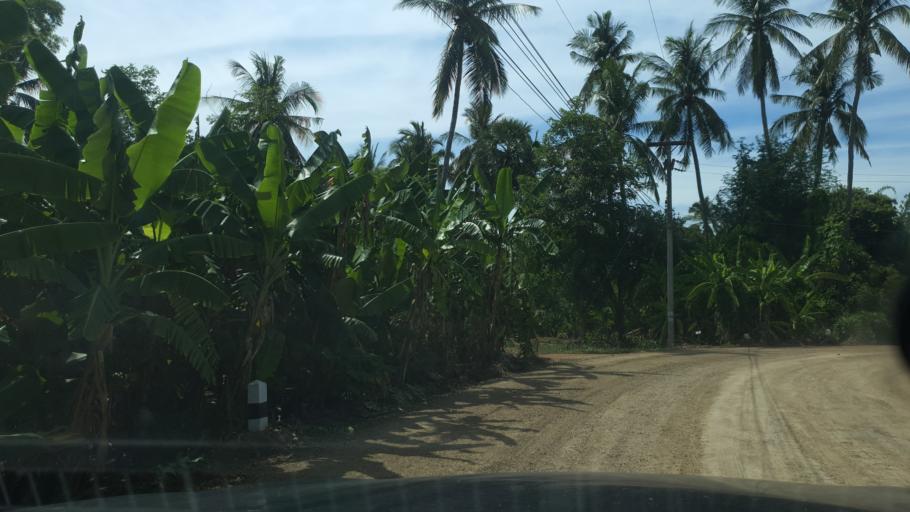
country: TH
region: Sukhothai
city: Si Samrong
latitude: 17.2105
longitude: 99.7194
